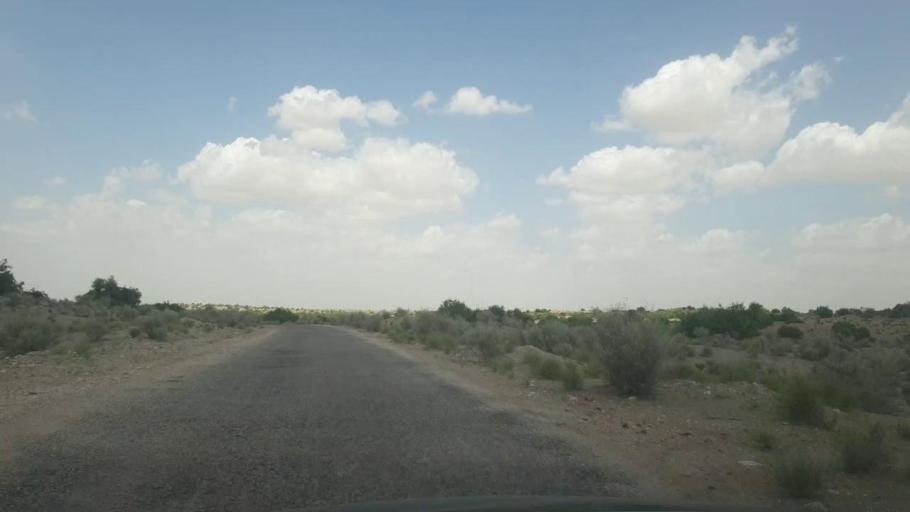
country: PK
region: Sindh
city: Kot Diji
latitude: 27.2234
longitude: 69.1089
